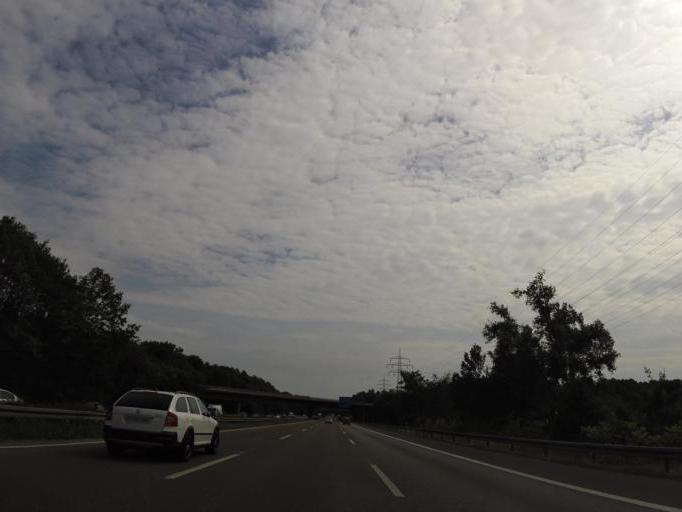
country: DE
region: Hesse
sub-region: Regierungsbezirk Darmstadt
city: Neu Isenburg
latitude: 50.0560
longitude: 8.7238
